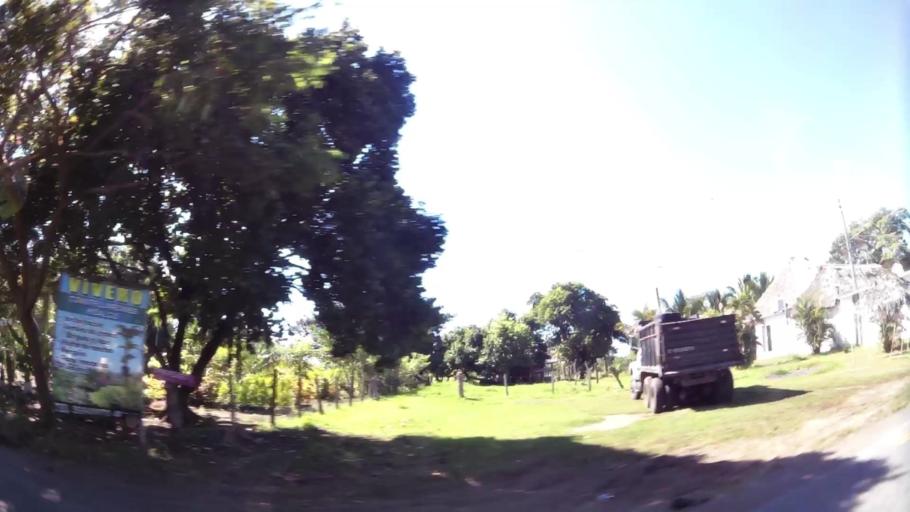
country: GT
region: Santa Rosa
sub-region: Municipio de Taxisco
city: Taxisco
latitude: 13.9104
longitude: -90.5275
